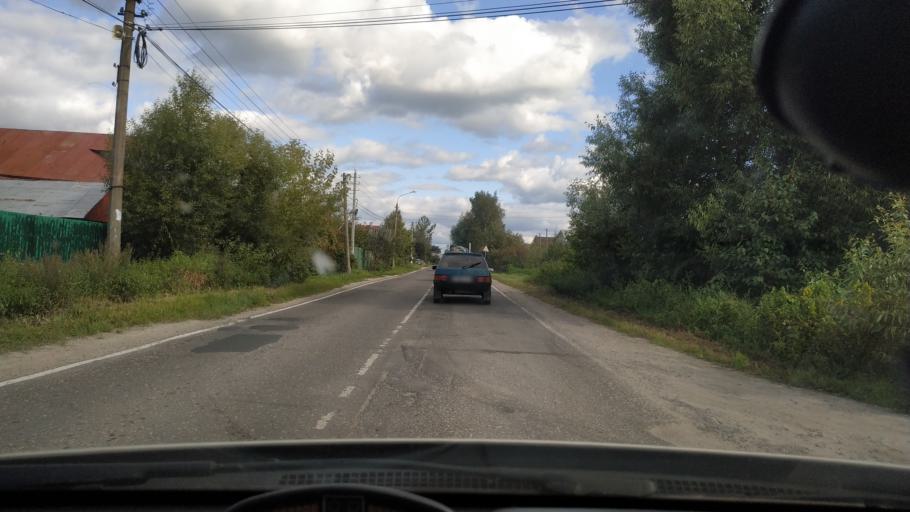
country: RU
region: Moskovskaya
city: Fryazevo
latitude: 55.7244
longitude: 38.4526
